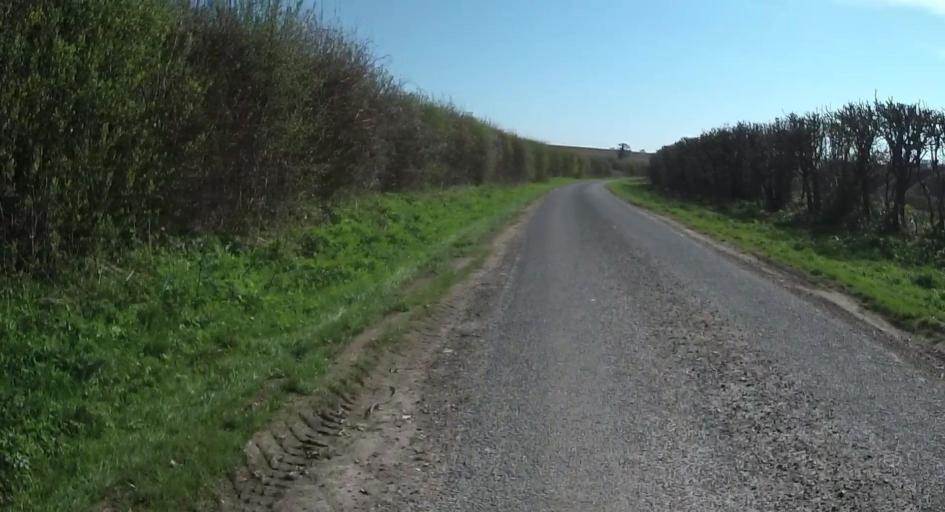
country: GB
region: England
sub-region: Hampshire
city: Highclere
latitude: 51.2670
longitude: -1.3905
